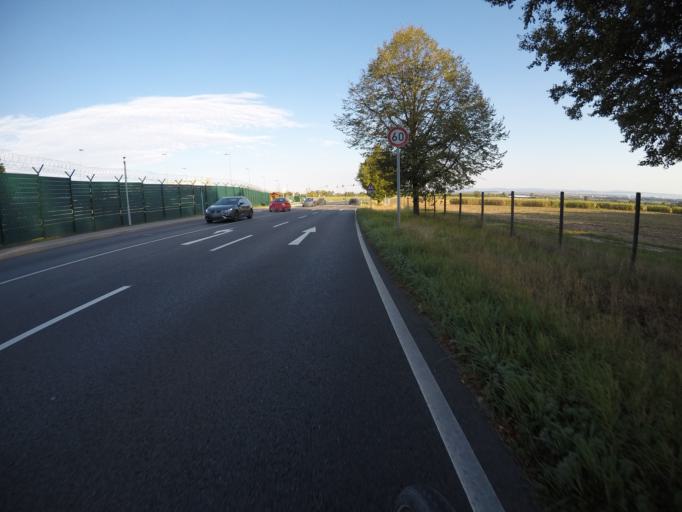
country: DE
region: Baden-Wuerttemberg
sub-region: Regierungsbezirk Stuttgart
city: Leinfelden-Echterdingen
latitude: 48.7215
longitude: 9.1799
